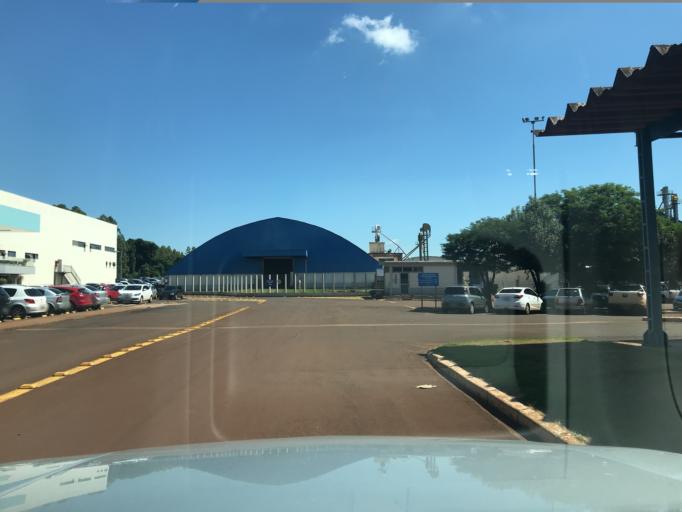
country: BR
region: Parana
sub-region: Palotina
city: Palotina
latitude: -24.2805
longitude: -53.8308
